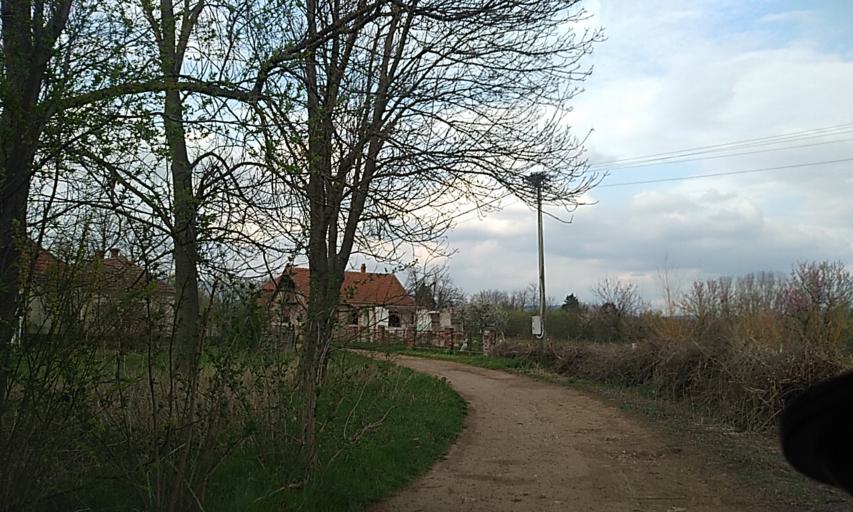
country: RS
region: Central Serbia
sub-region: Nisavski Okrug
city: Razanj
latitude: 43.5943
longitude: 21.6077
